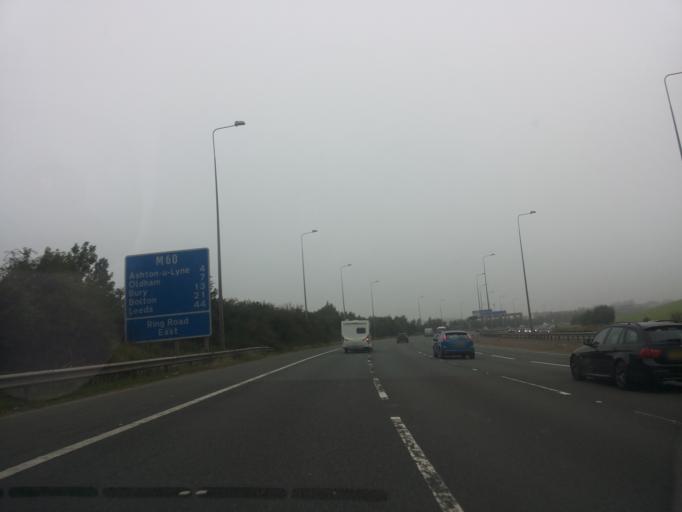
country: GB
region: England
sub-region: Borough of Tameside
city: Droylsden
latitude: 53.4648
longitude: -2.1397
